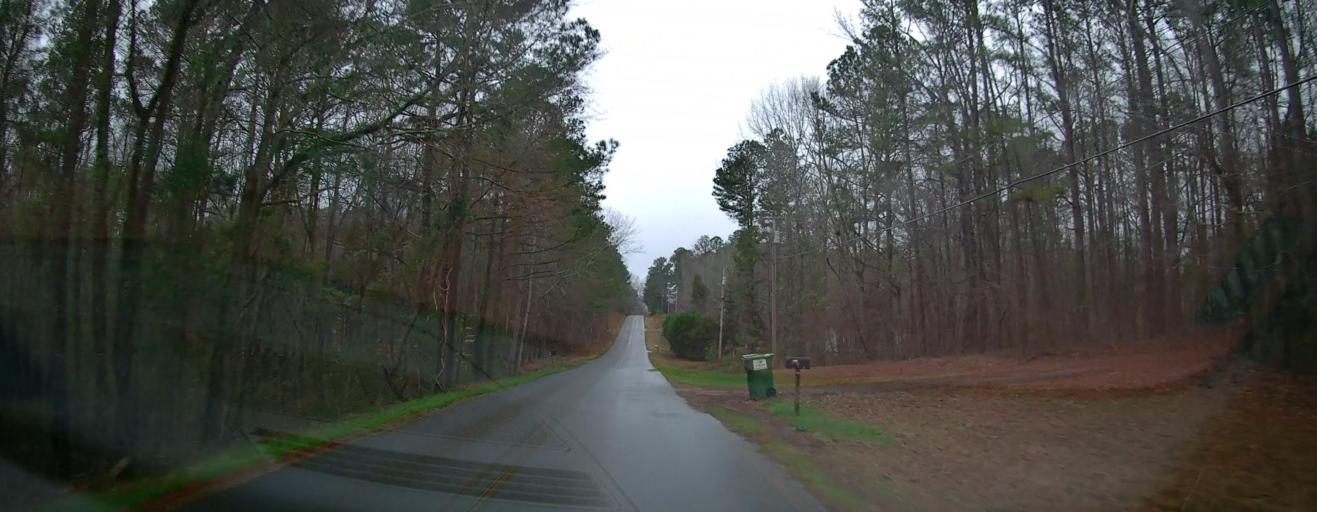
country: US
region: Georgia
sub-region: Monroe County
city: Forsyth
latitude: 33.0903
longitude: -83.9437
